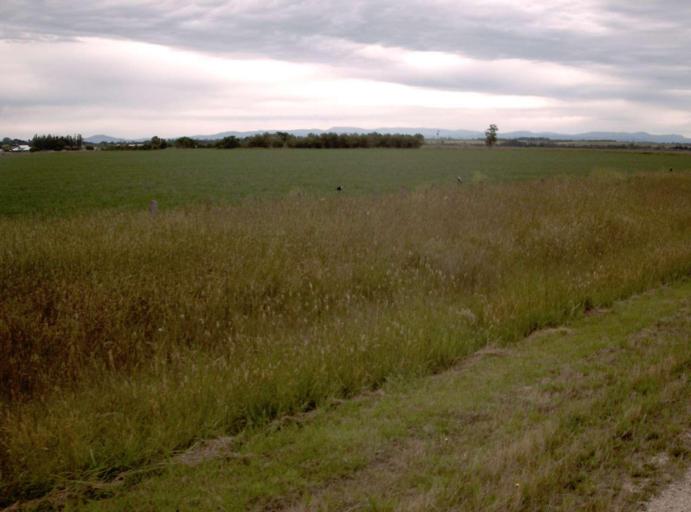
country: AU
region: Victoria
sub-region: Wellington
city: Sale
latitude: -38.0455
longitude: 147.1753
